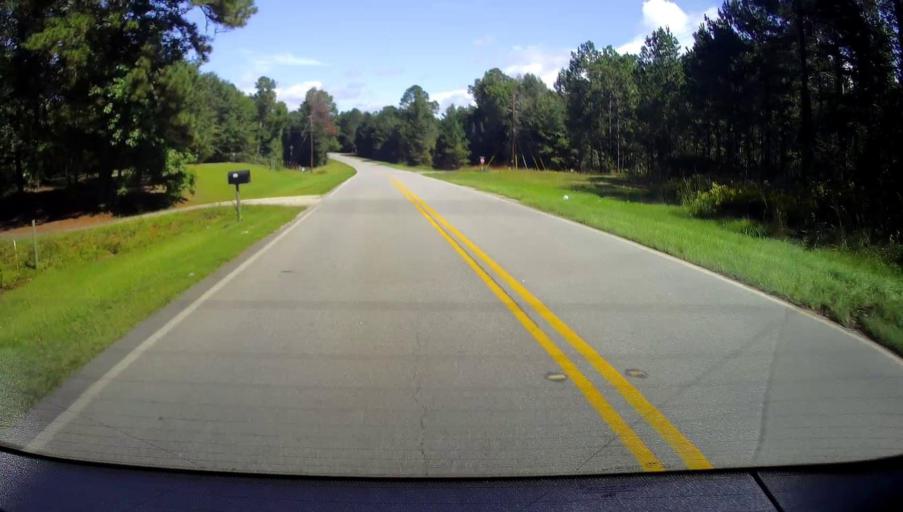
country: US
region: Georgia
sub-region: Houston County
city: Warner Robins
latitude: 32.7159
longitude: -83.5358
